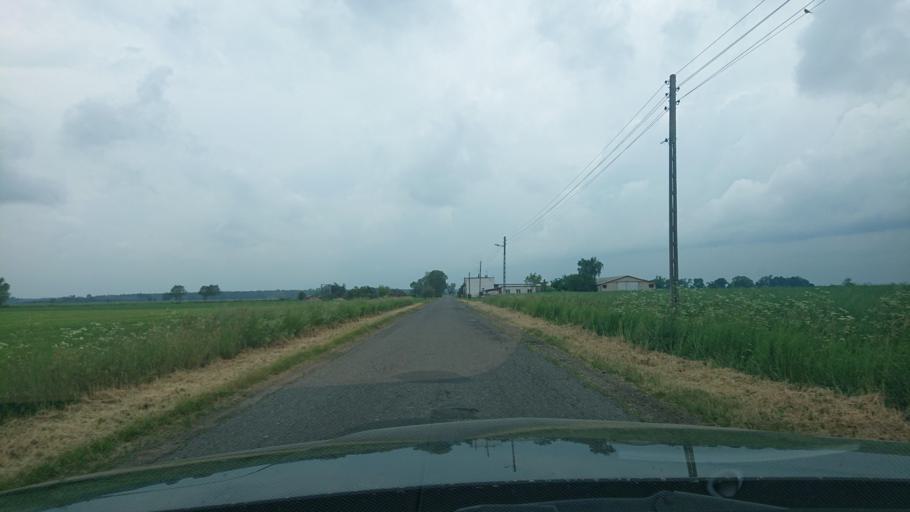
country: PL
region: Greater Poland Voivodeship
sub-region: Powiat gnieznienski
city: Czerniejewo
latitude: 52.4595
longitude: 17.5321
